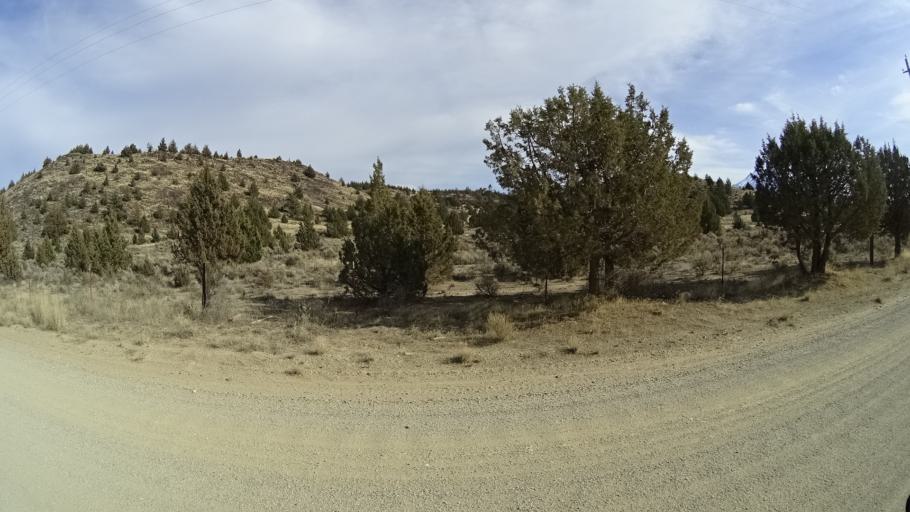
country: US
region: California
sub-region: Siskiyou County
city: Weed
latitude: 41.5653
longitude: -122.4681
